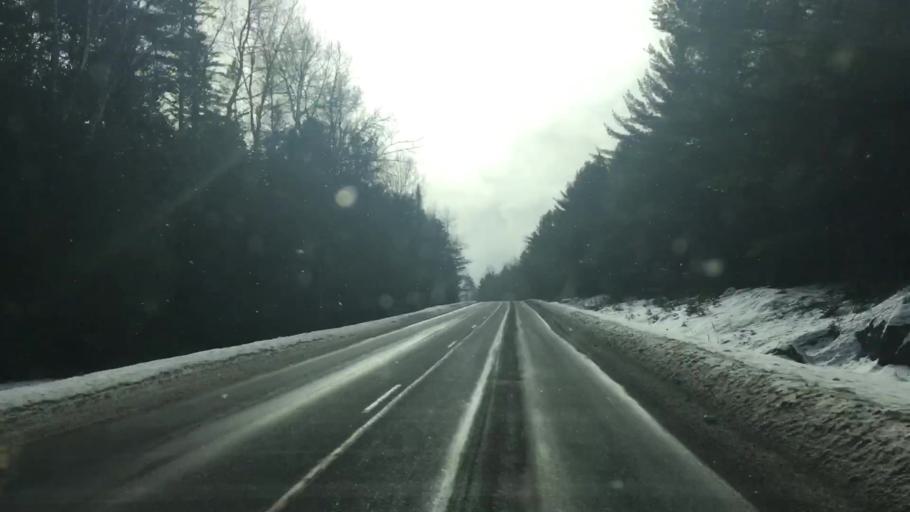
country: US
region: Maine
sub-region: Washington County
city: Calais
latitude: 45.0695
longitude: -67.3312
